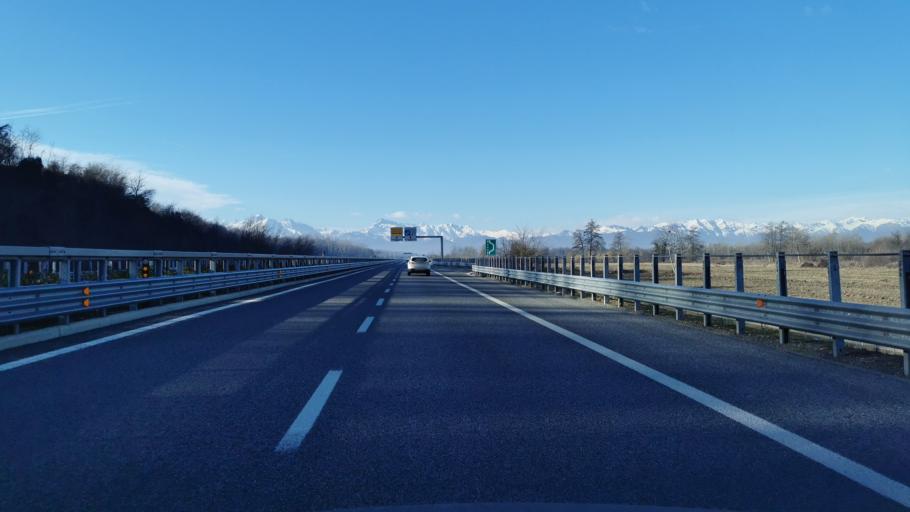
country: IT
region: Piedmont
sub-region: Provincia di Cuneo
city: Castelletto Stura
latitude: 44.4400
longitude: 7.6258
